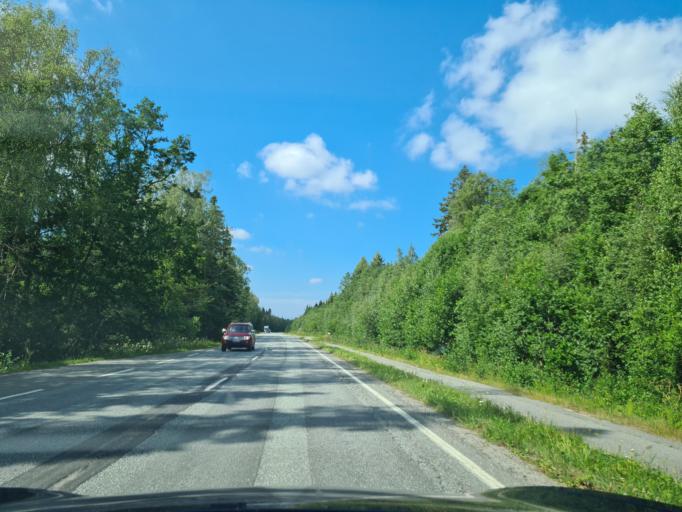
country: FI
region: Ostrobothnia
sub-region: Vaasa
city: Vaasa
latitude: 63.1974
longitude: 21.5422
